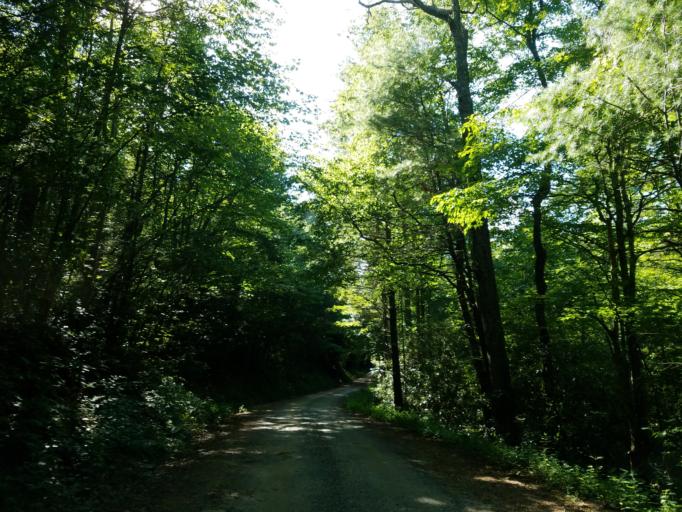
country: US
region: Georgia
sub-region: Dawson County
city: Dawsonville
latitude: 34.5871
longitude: -84.1897
